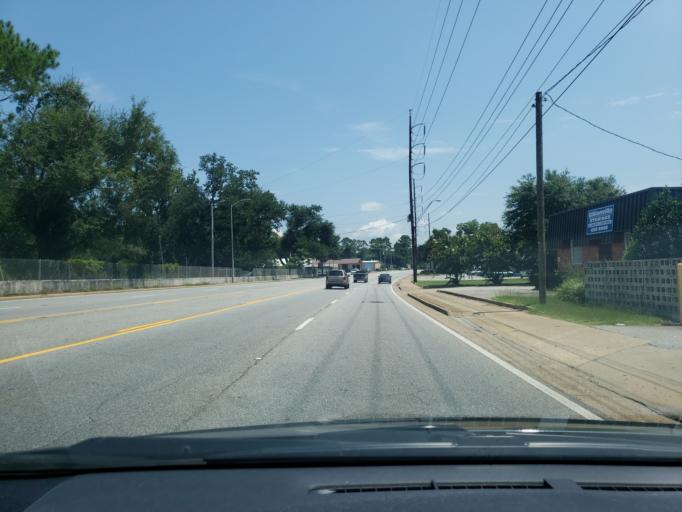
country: US
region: Georgia
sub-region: Dougherty County
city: Albany
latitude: 31.5812
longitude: -84.1886
